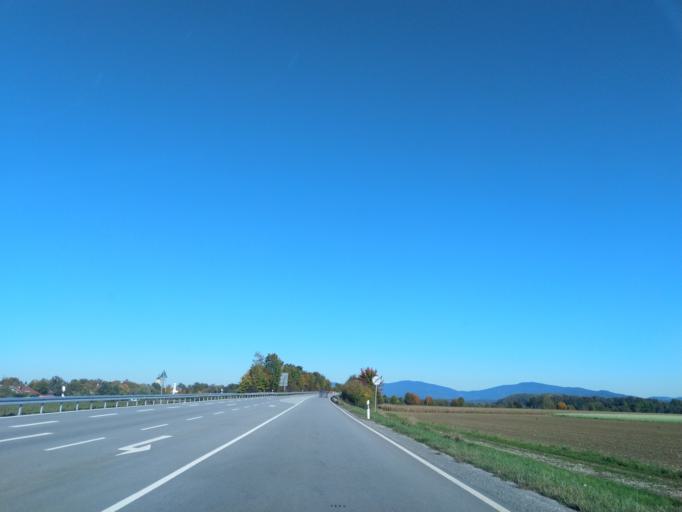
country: DE
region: Bavaria
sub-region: Lower Bavaria
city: Plattling
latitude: 48.7990
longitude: 12.9041
